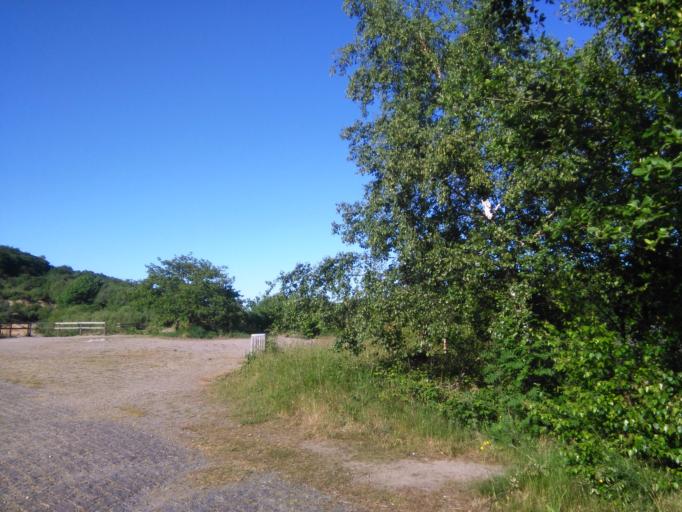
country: DK
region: Capital Region
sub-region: Bornholm Kommune
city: Ronne
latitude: 55.2816
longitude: 14.7607
